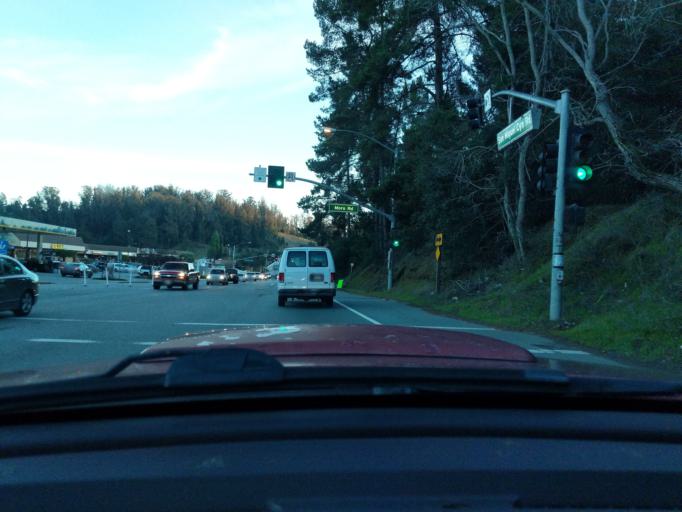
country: US
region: California
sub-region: Monterey County
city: Prunedale
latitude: 36.8028
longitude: -121.6668
